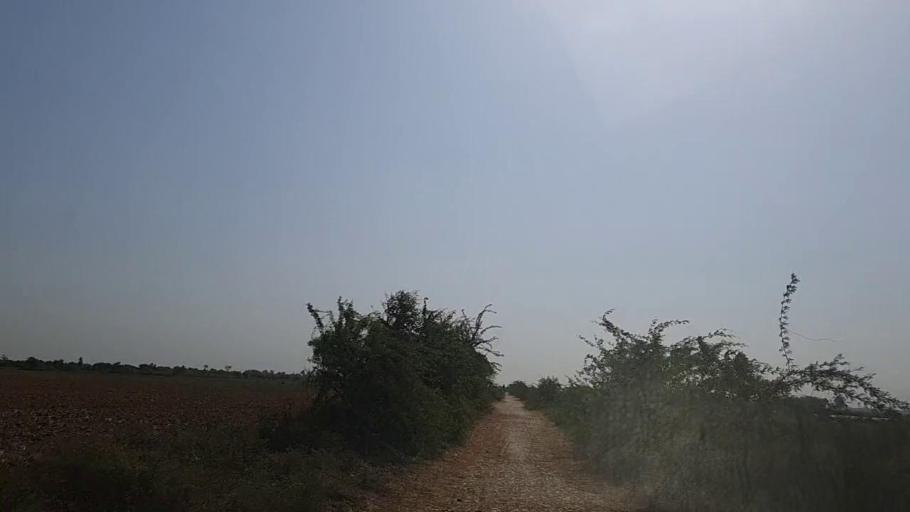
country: PK
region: Sindh
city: Daro Mehar
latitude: 24.7158
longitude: 68.1185
